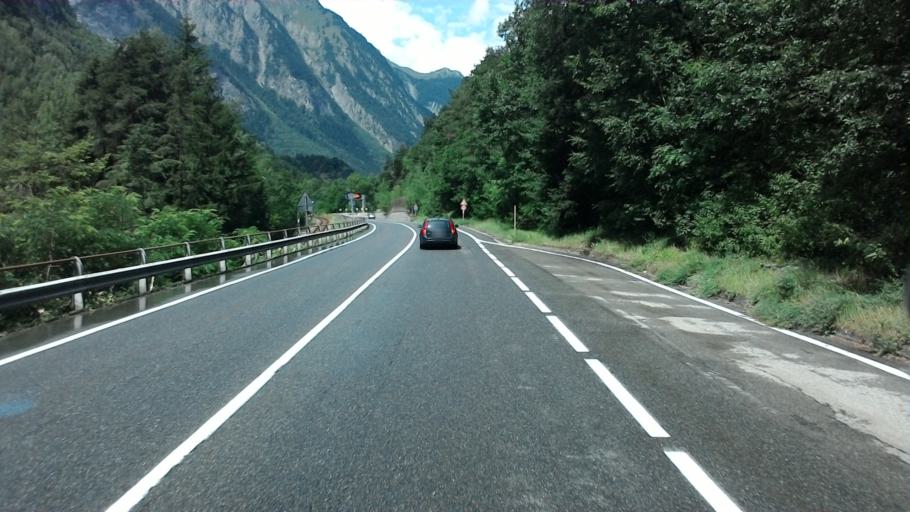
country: IT
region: Aosta Valley
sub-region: Valle d'Aosta
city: Pre Saint Didier
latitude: 45.7611
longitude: 7.0135
